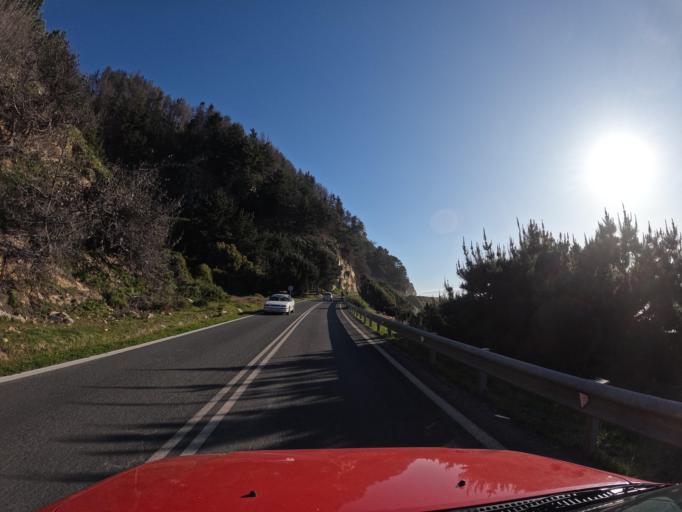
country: CL
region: Maule
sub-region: Provincia de Talca
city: Constitucion
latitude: -35.3488
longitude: -72.4387
